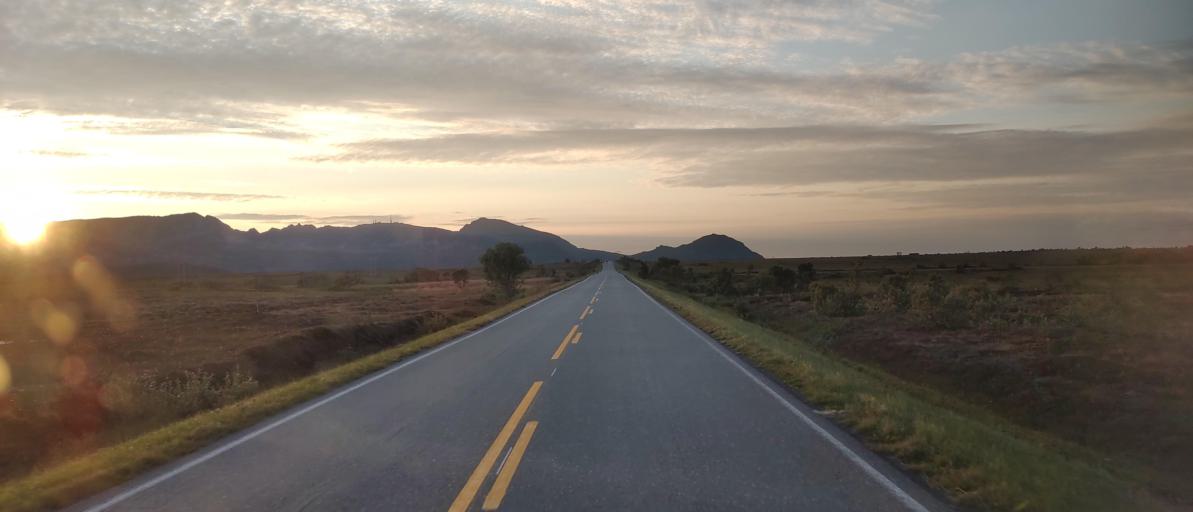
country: NO
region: Nordland
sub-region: Andoy
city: Andenes
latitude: 69.2478
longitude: 16.1126
